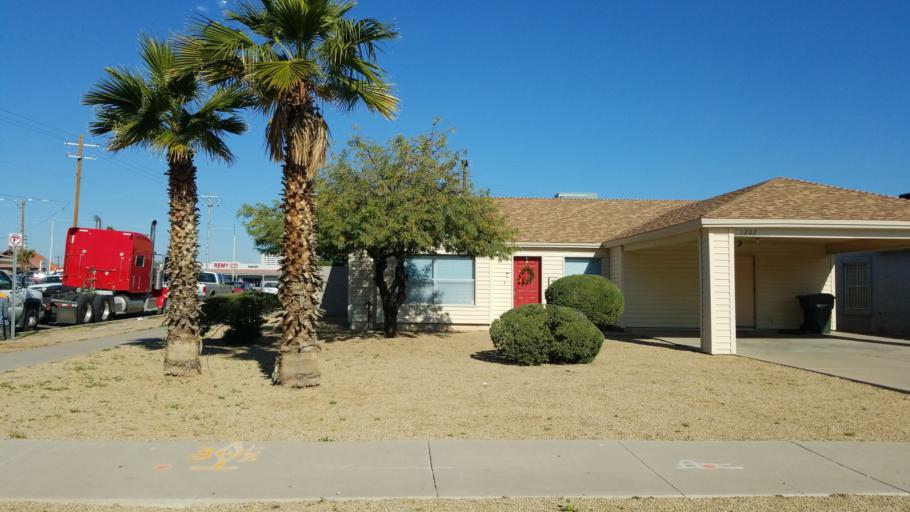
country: US
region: Arizona
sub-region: Maricopa County
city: Phoenix
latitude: 33.4505
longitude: -112.0563
